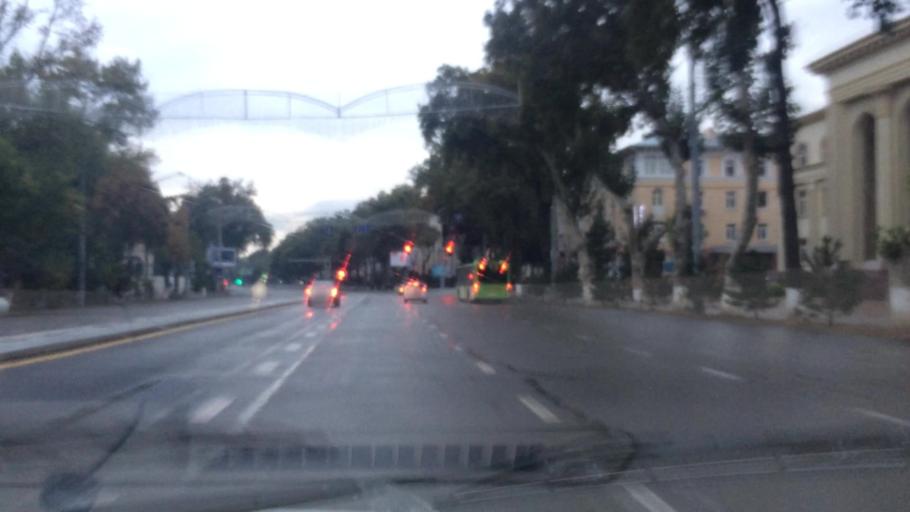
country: UZ
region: Toshkent Shahri
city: Tashkent
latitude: 41.3201
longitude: 69.2664
